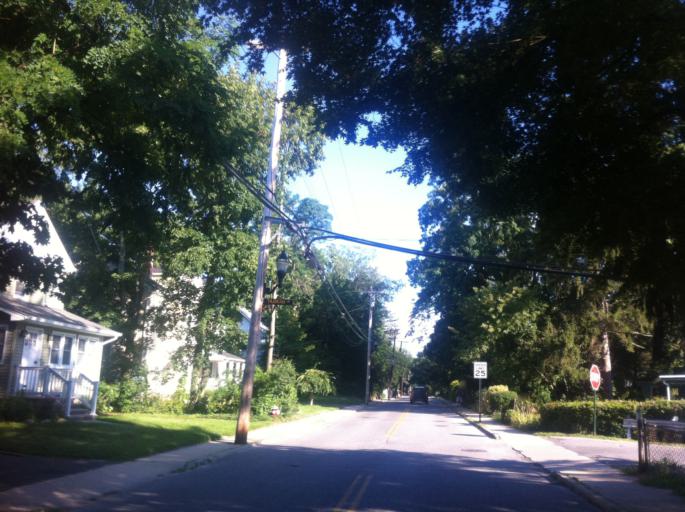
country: US
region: New York
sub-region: Nassau County
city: Bayville
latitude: 40.9060
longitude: -73.5718
